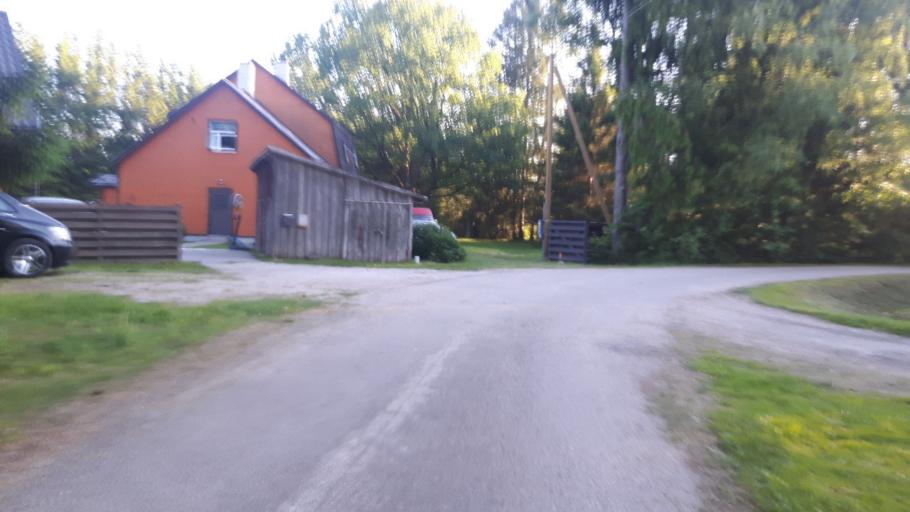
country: EE
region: Raplamaa
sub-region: Jaervakandi vald
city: Jarvakandi
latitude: 58.7583
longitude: 24.9465
